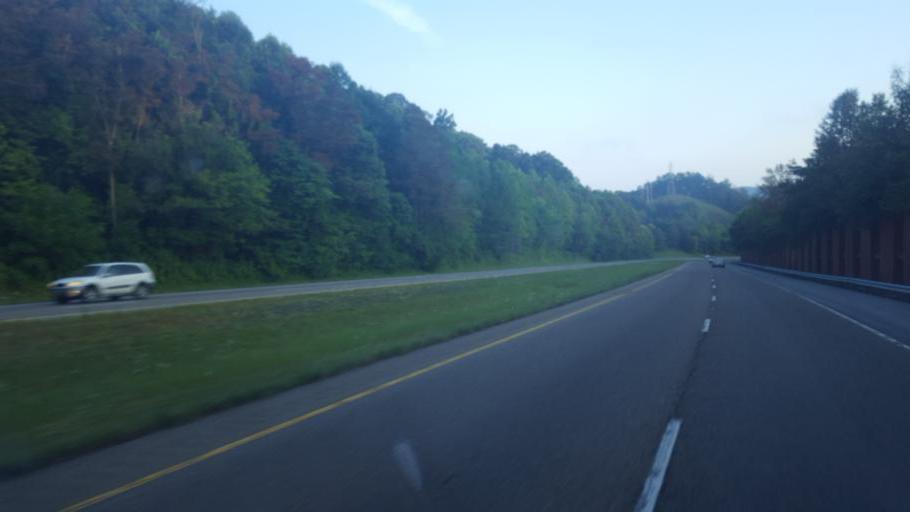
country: US
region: Tennessee
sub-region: Sullivan County
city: Kingsport
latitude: 36.5797
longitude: -82.5792
